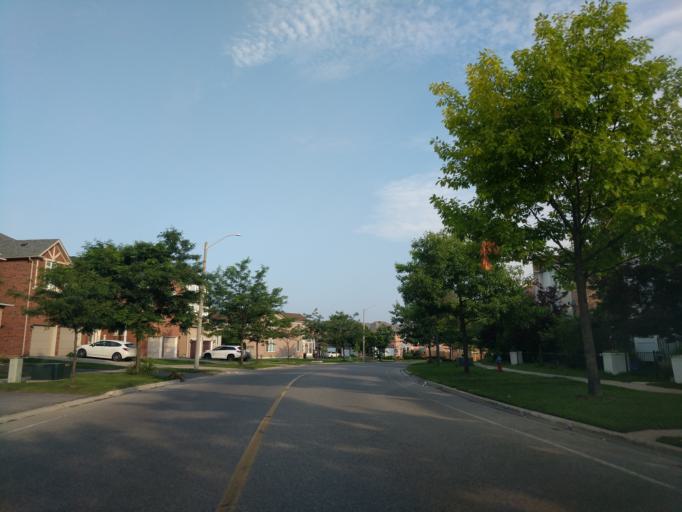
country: CA
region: Ontario
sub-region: York
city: Richmond Hill
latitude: 43.8855
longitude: -79.4062
